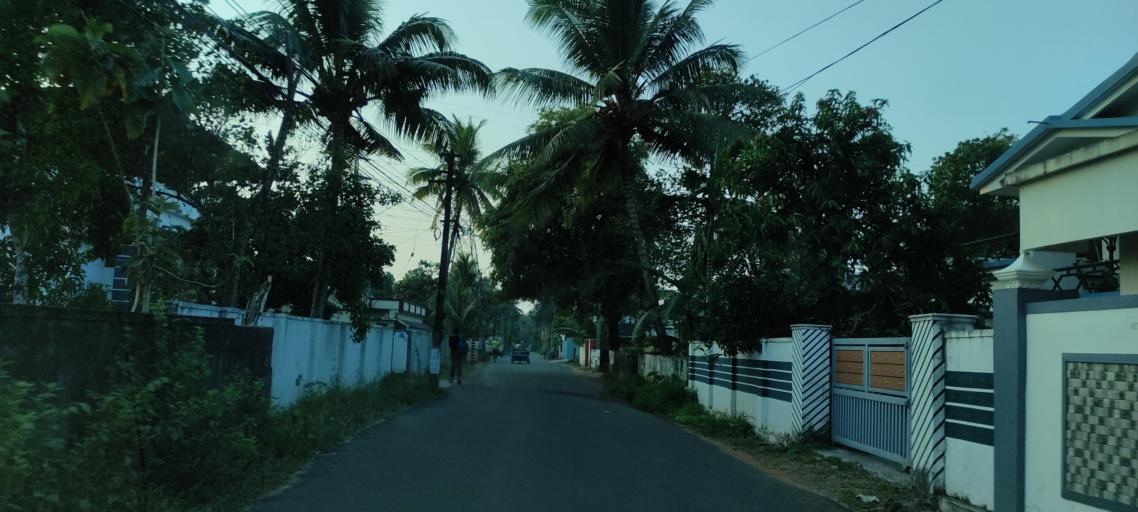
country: IN
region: Kerala
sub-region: Alappuzha
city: Alleppey
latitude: 9.4273
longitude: 76.3480
